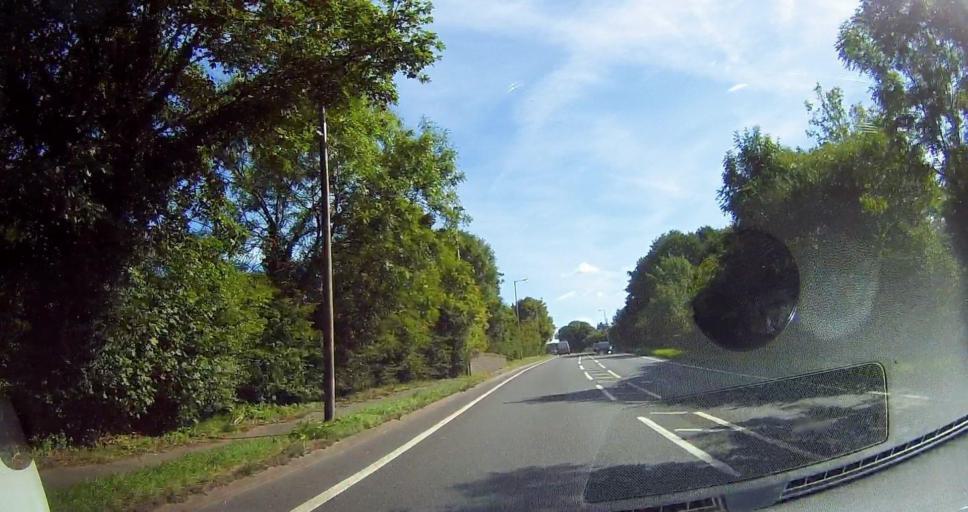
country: GB
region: England
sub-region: Staffordshire
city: Great Wyrley
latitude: 52.6697
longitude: -2.0113
